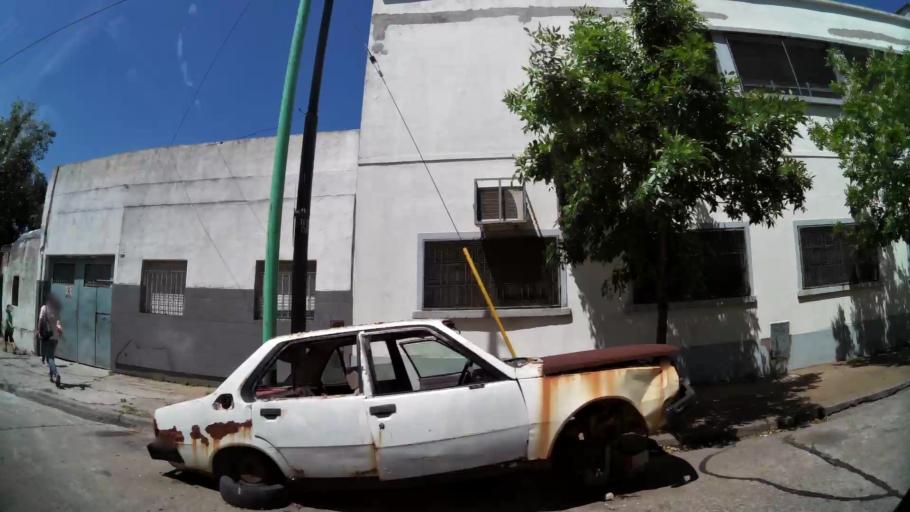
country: AR
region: Buenos Aires
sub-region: Partido de Avellaneda
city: Avellaneda
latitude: -34.6527
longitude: -58.4113
